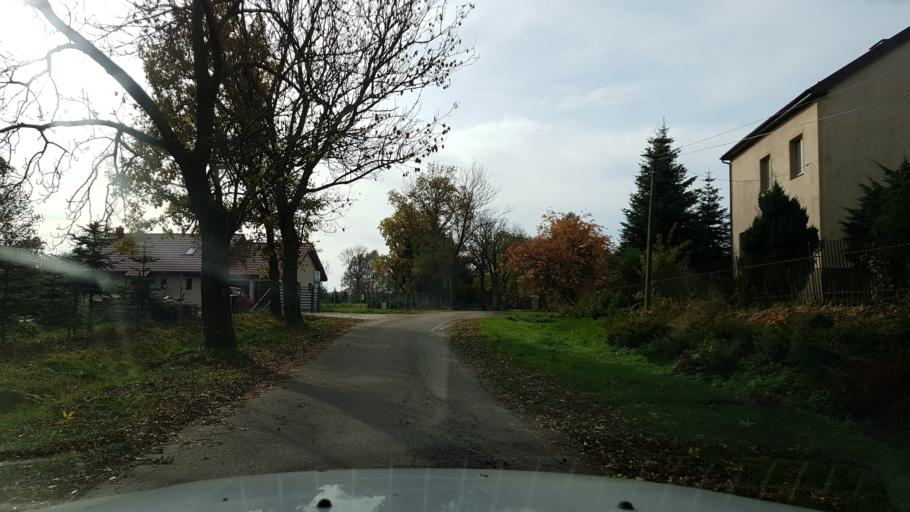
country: PL
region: West Pomeranian Voivodeship
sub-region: Powiat swidwinski
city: Polczyn-Zdroj
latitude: 53.7377
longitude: 16.0358
